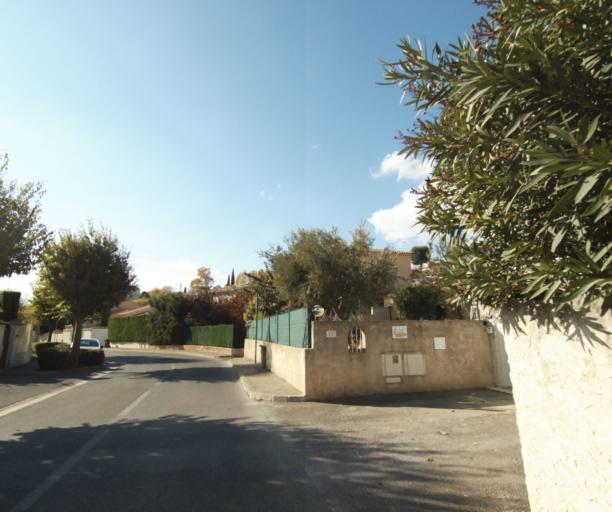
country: FR
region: Provence-Alpes-Cote d'Azur
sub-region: Departement des Bouches-du-Rhone
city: Plan-de-Cuques
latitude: 43.3454
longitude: 5.4550
